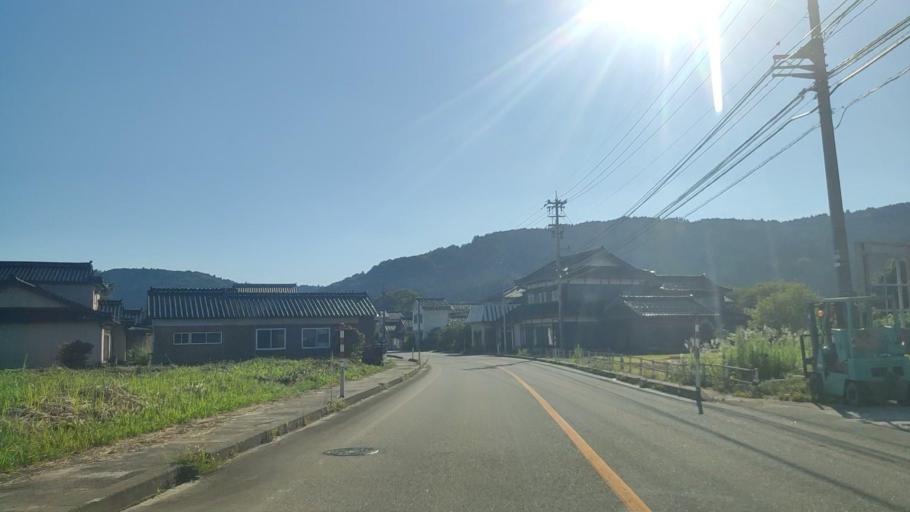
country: JP
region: Ishikawa
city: Nanao
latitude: 37.1466
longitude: 136.8736
